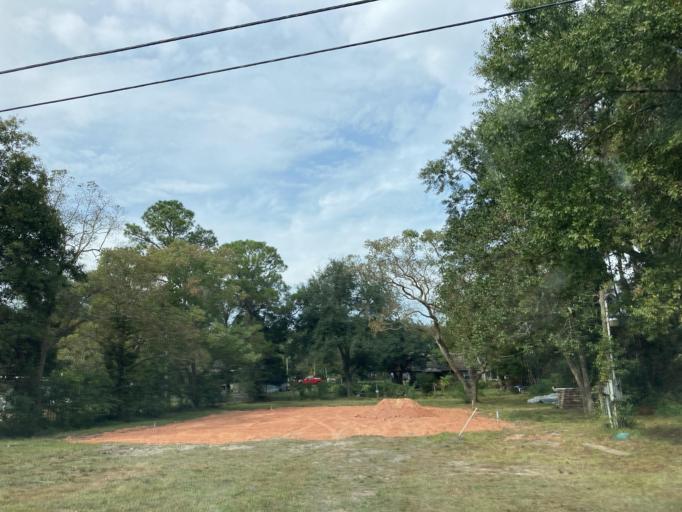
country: US
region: Mississippi
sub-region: Jackson County
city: Saint Martin
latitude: 30.4704
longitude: -88.8468
